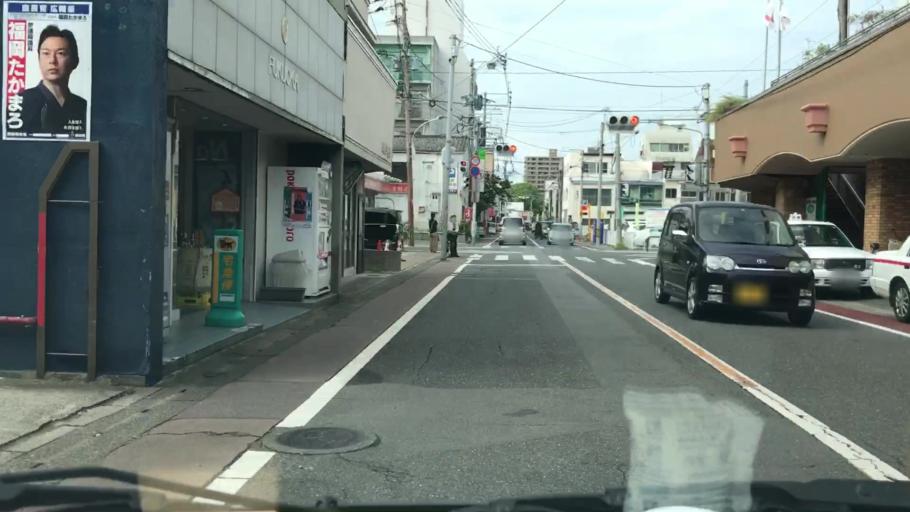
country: JP
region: Saga Prefecture
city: Saga-shi
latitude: 33.2523
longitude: 130.2992
